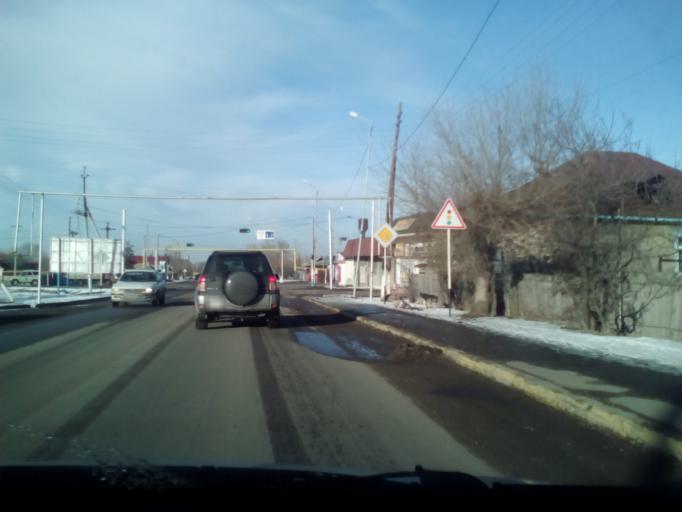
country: KZ
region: Almaty Oblysy
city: Burunday
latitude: 43.1782
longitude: 76.4143
